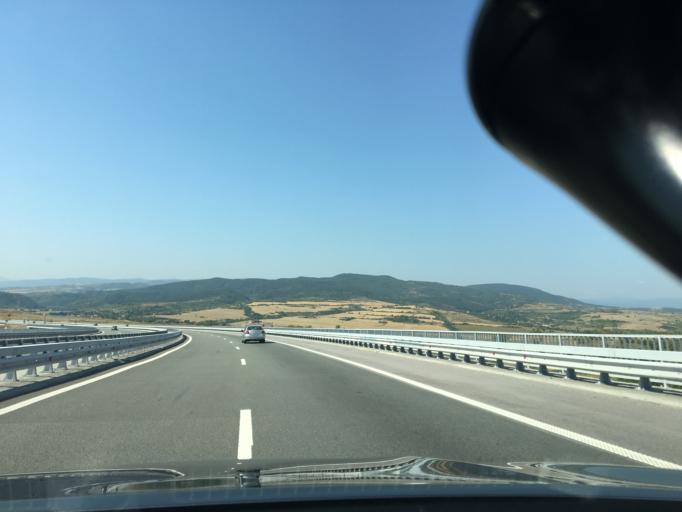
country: BG
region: Kyustendil
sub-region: Obshtina Dupnitsa
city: Dupnitsa
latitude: 42.2710
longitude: 23.0724
